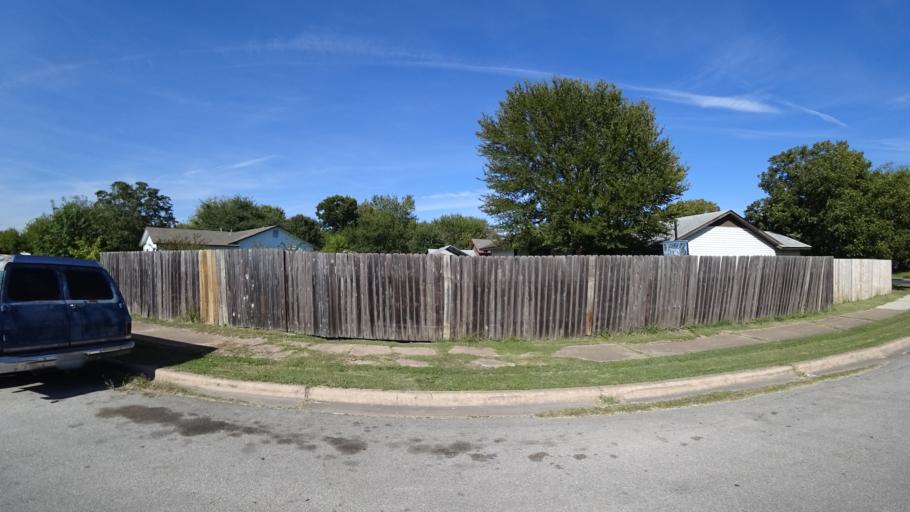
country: US
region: Texas
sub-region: Travis County
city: Onion Creek
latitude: 30.1946
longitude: -97.7503
